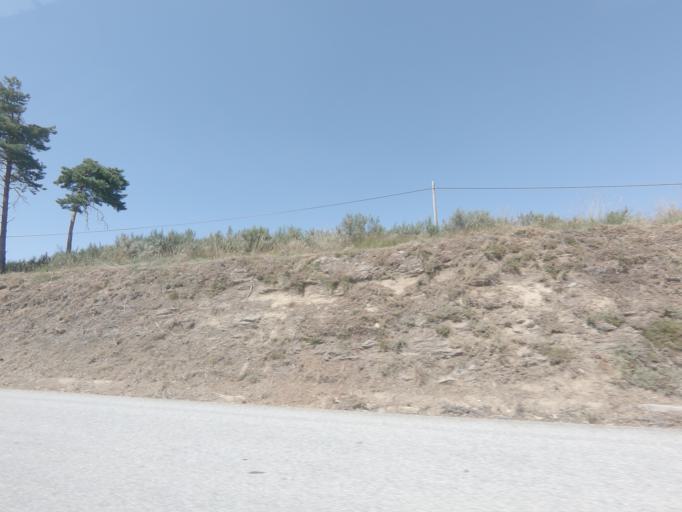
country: PT
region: Viseu
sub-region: Tarouca
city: Tarouca
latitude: 40.9862
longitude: -7.8028
